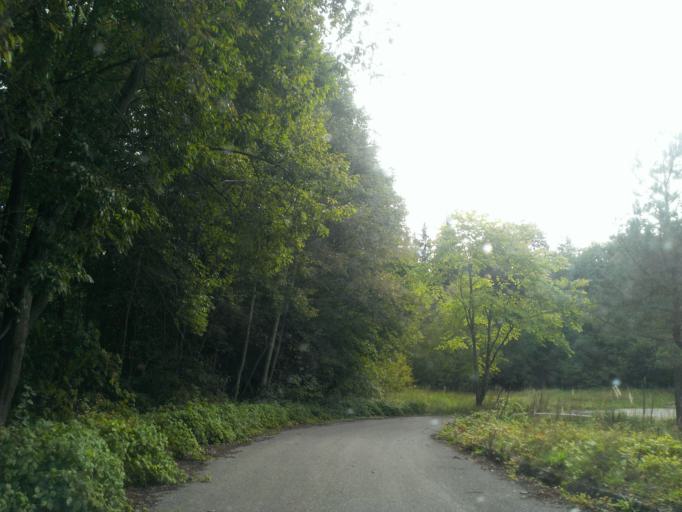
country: LV
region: Sigulda
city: Sigulda
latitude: 57.1788
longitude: 24.8239
